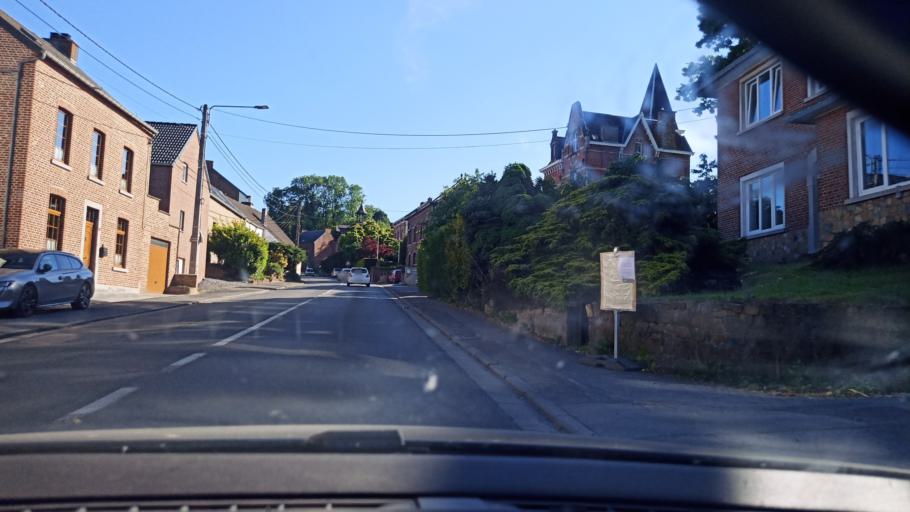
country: BE
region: Wallonia
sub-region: Province du Hainaut
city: Lobbes
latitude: 50.3437
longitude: 4.2639
